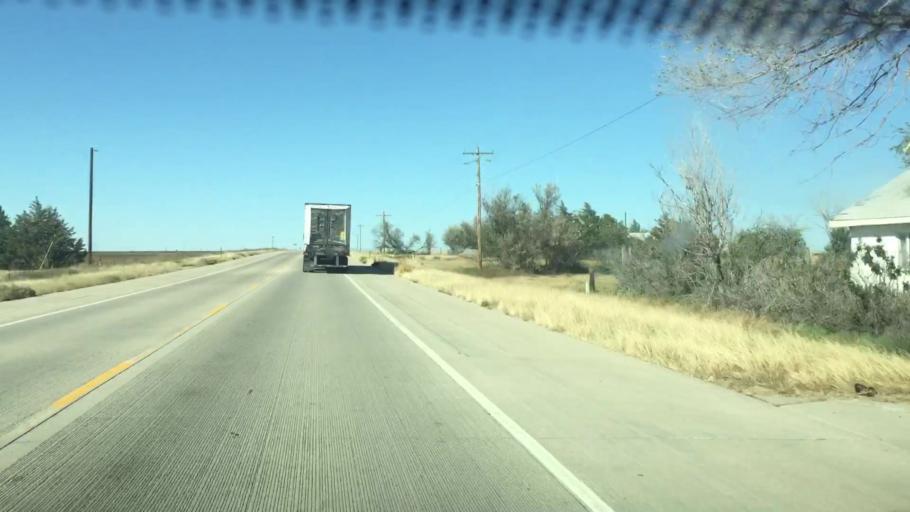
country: US
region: Colorado
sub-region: Kiowa County
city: Eads
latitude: 38.4638
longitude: -102.7307
